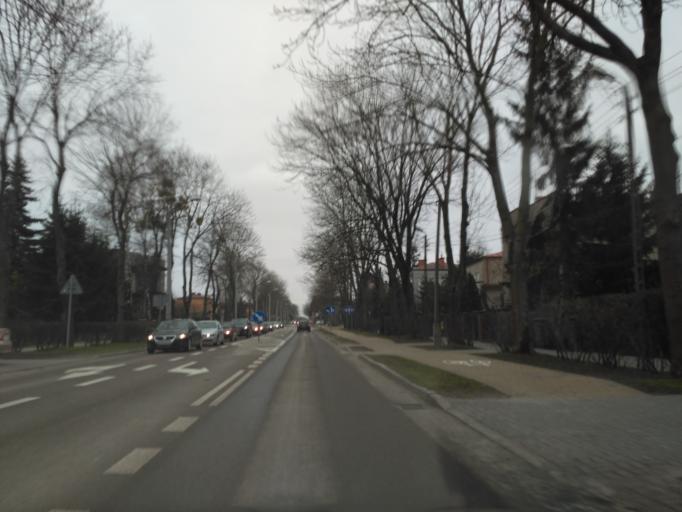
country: PL
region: Lublin Voivodeship
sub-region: Chelm
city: Chelm
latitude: 51.1268
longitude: 23.4905
